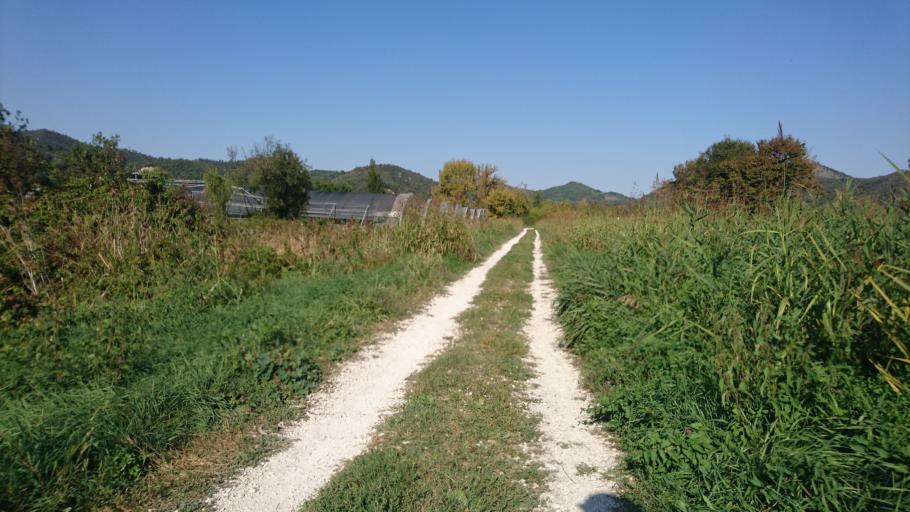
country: IT
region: Veneto
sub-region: Provincia di Padova
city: Galzignano
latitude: 45.2990
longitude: 11.7431
